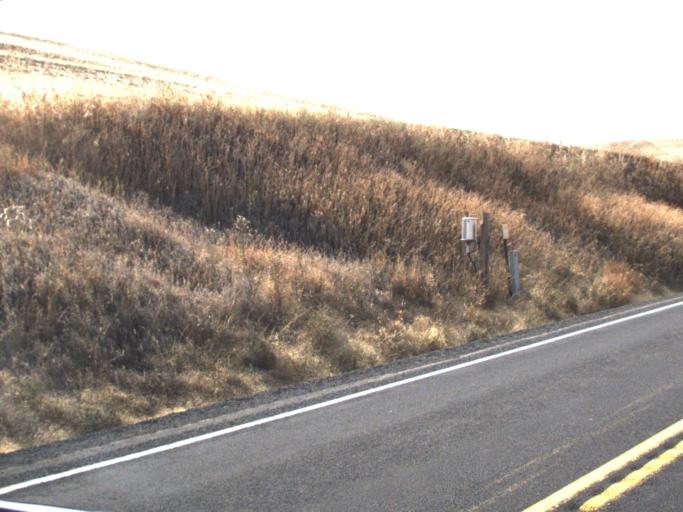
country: US
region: Washington
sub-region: Whitman County
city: Pullman
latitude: 46.9485
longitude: -117.0929
